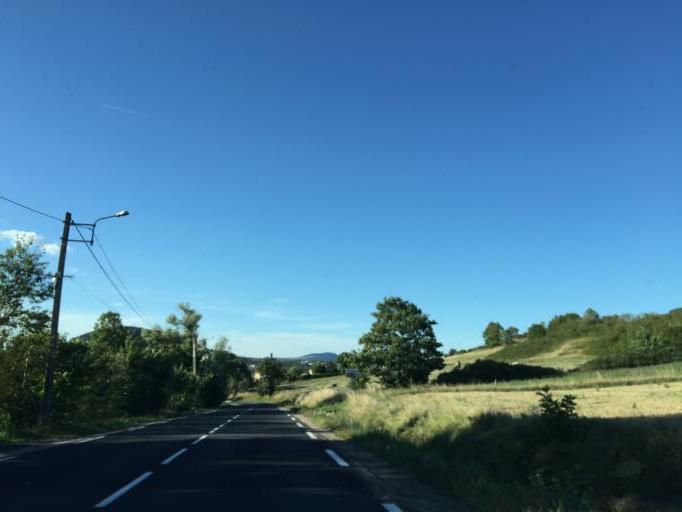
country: FR
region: Auvergne
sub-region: Departement de la Haute-Loire
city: Espaly-Saint-Marcel
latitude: 45.0375
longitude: 3.8651
